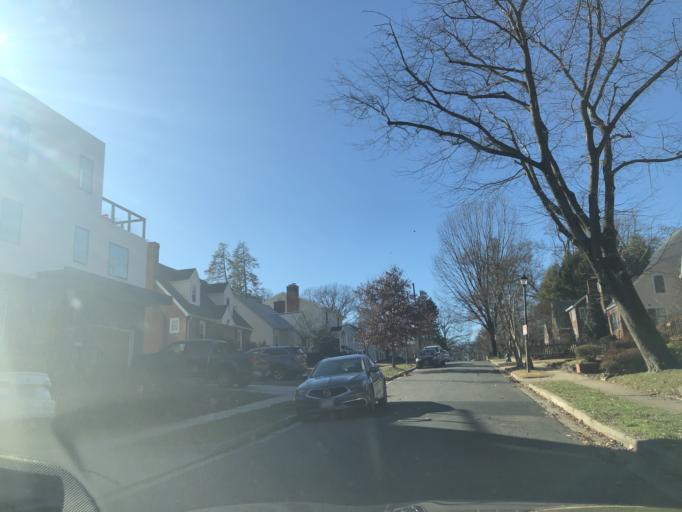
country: US
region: Virginia
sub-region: Arlington County
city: Arlington
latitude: 38.8866
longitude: -77.1234
